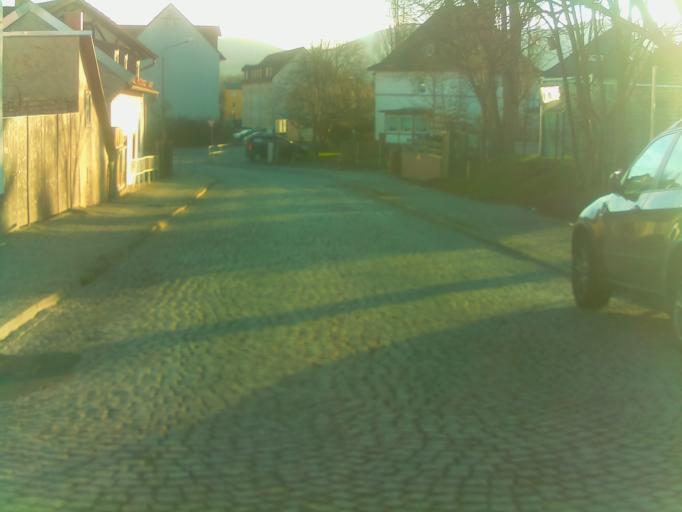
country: DE
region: Thuringia
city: Rudolstadt
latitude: 50.6905
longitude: 11.3235
